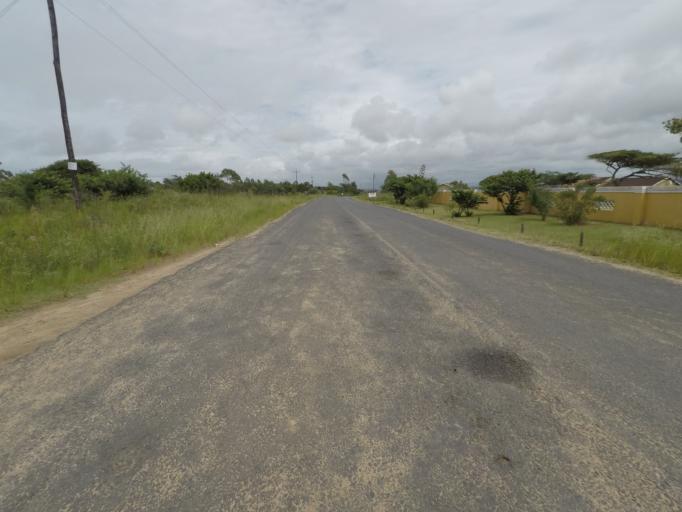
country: ZA
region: KwaZulu-Natal
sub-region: uThungulu District Municipality
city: eSikhawini
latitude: -28.9127
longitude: 31.8591
